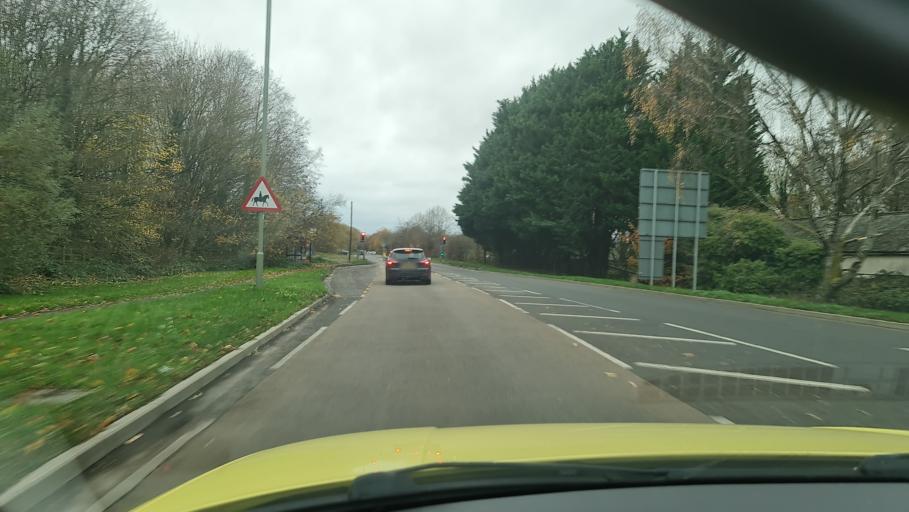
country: GB
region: England
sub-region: Bracknell Forest
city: Sandhurst
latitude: 51.3366
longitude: -0.8062
